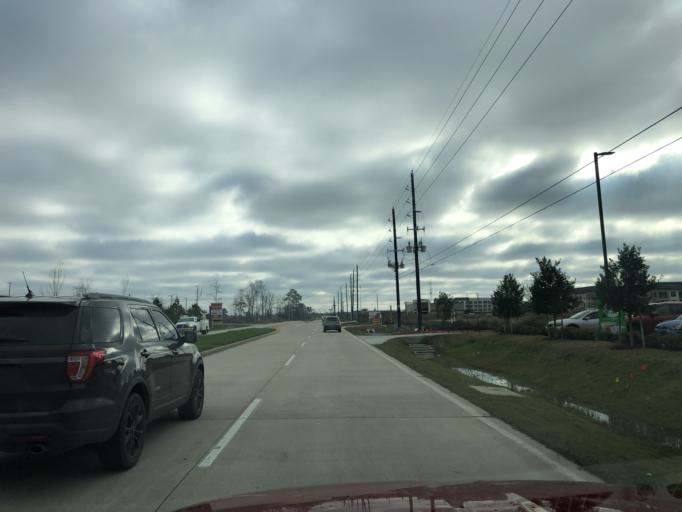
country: US
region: Texas
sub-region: Harris County
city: Spring
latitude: 30.0827
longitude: -95.4485
